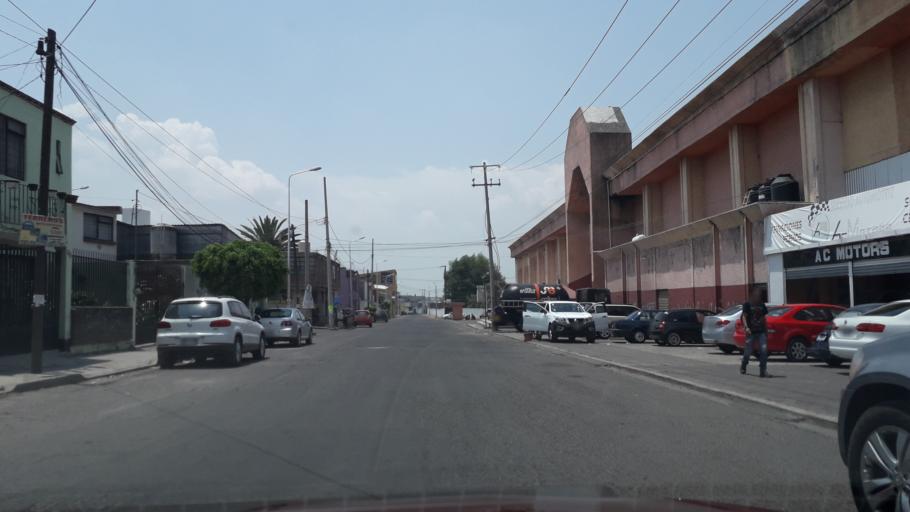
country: MX
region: Puebla
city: Puebla
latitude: 19.0486
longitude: -98.1661
